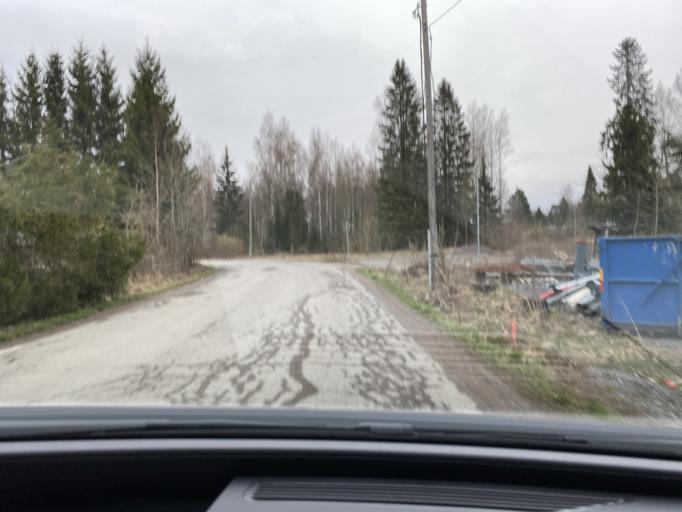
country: FI
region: Satakunta
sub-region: Pori
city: Huittinen
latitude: 61.1912
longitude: 22.7002
